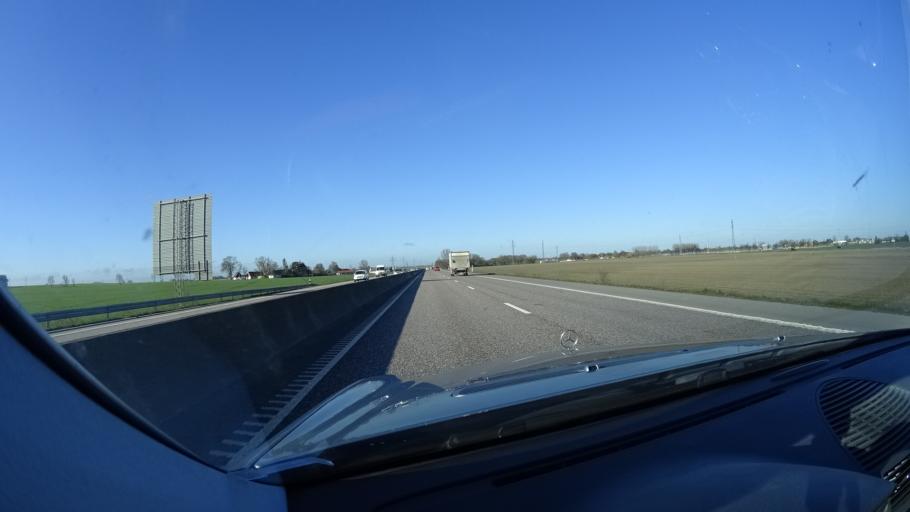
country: SE
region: Skane
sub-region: Staffanstorps Kommun
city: Hjaerup
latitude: 55.6696
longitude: 13.1664
